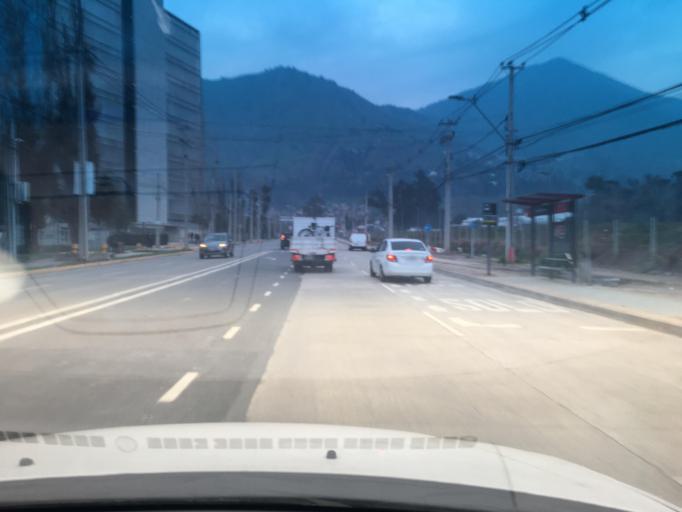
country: CL
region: Santiago Metropolitan
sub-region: Provincia de Santiago
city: Santiago
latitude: -33.3838
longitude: -70.6213
